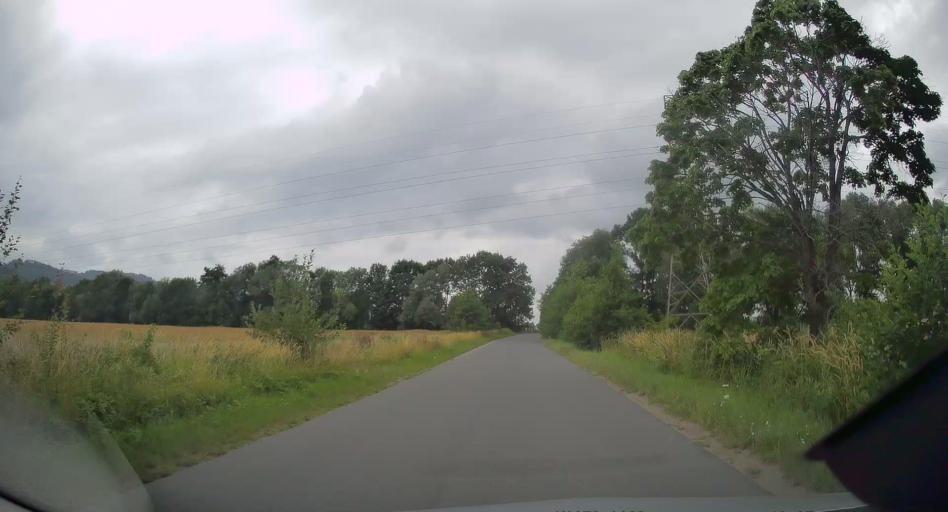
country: PL
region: Lower Silesian Voivodeship
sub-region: Powiat zabkowicki
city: Budzow
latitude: 50.5674
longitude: 16.6845
